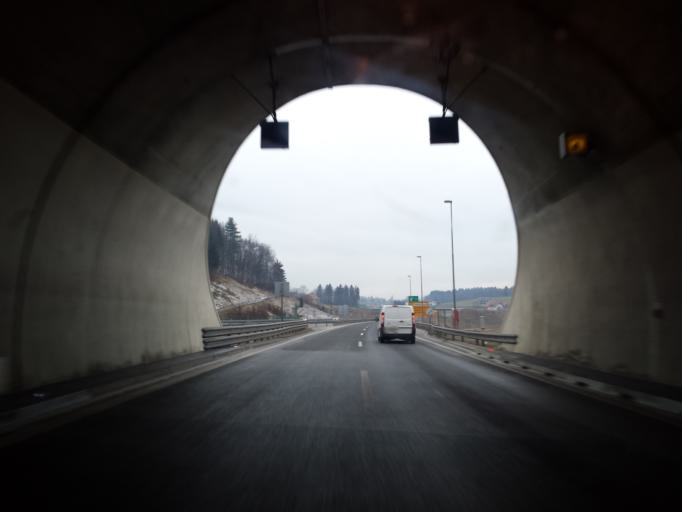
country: SI
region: Trebnje
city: Trebnje
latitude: 45.9052
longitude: 14.9800
